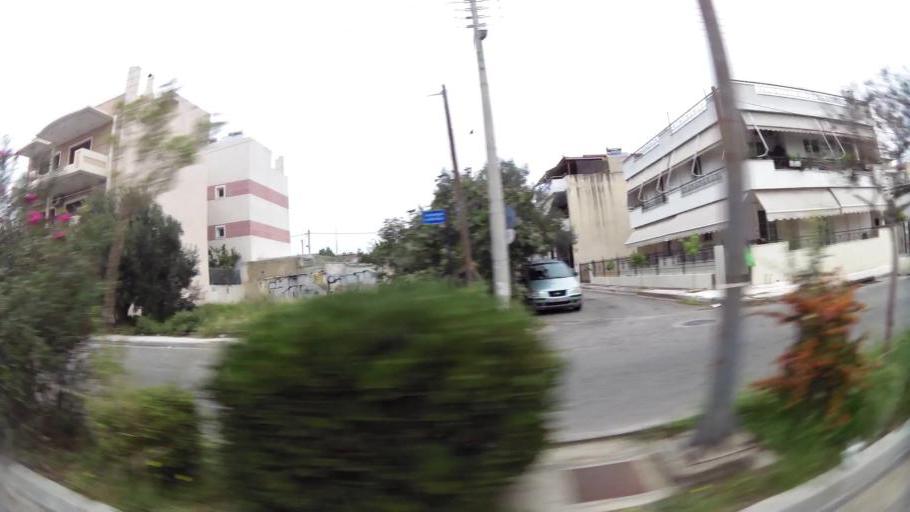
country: GR
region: Attica
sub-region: Nomarchia Athinas
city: Agioi Anargyroi
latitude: 38.0379
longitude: 23.7138
